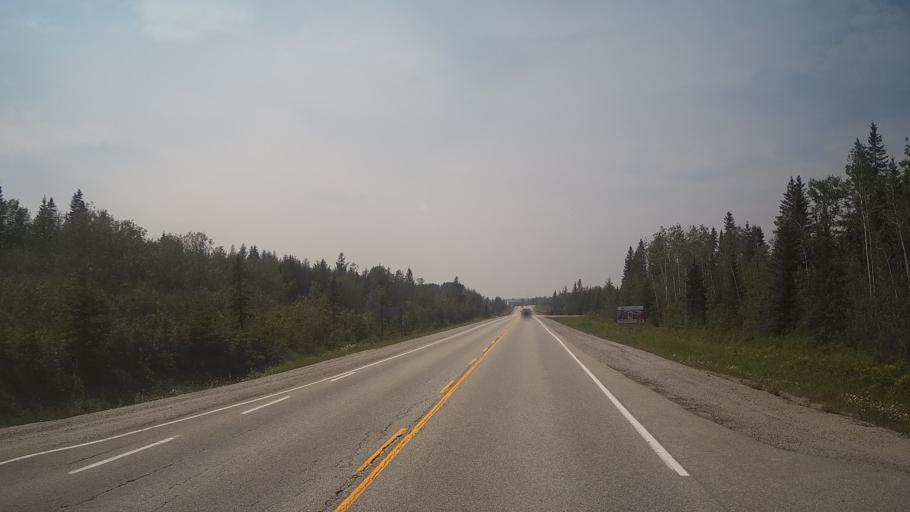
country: CA
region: Ontario
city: Kapuskasing
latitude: 49.3280
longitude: -82.0759
